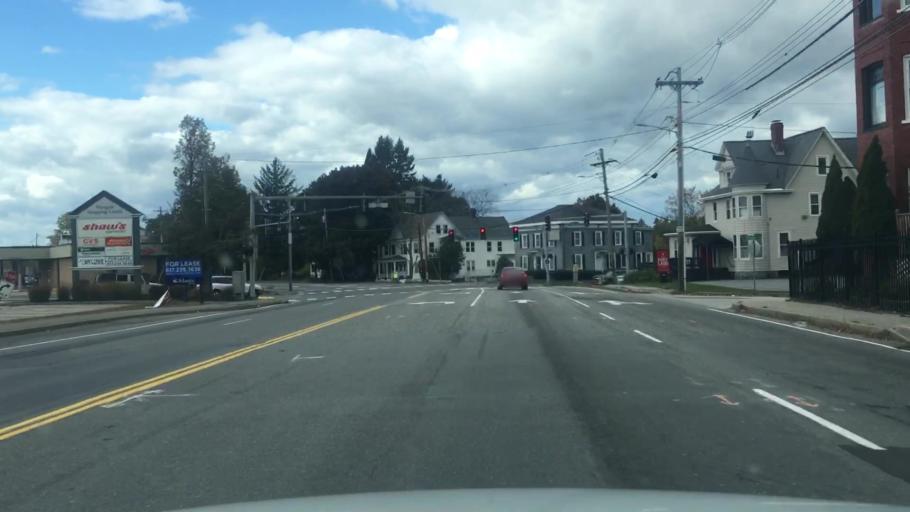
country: US
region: Maine
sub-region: Cumberland County
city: South Portland Gardens
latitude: 43.6589
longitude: -70.2957
